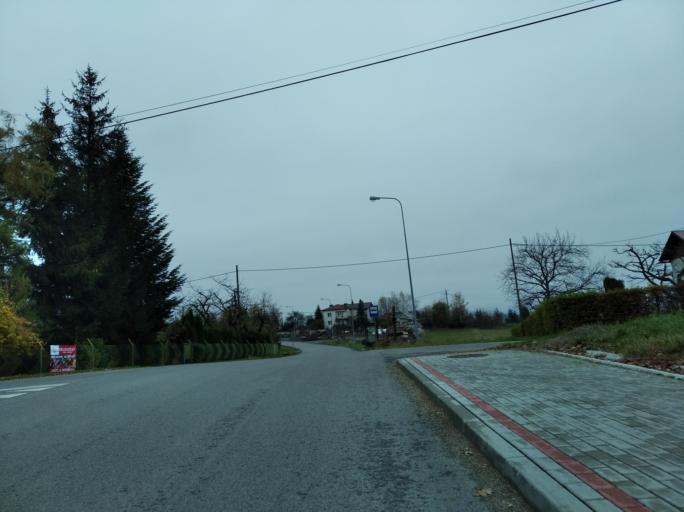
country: PL
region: Subcarpathian Voivodeship
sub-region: Powiat krosnienski
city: Jedlicze
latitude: 49.7282
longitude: 21.6527
